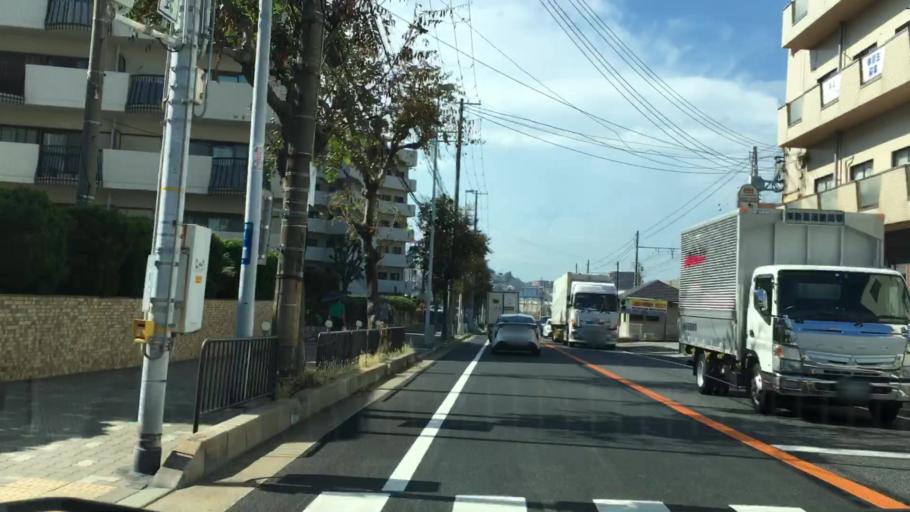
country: JP
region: Hyogo
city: Akashi
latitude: 34.6345
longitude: 135.0317
